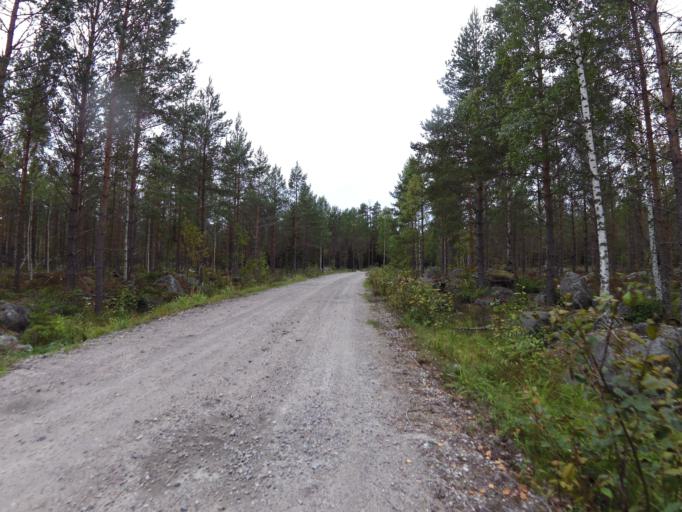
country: SE
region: Gaevleborg
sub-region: Gavle Kommun
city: Valbo
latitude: 60.7358
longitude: 17.0482
